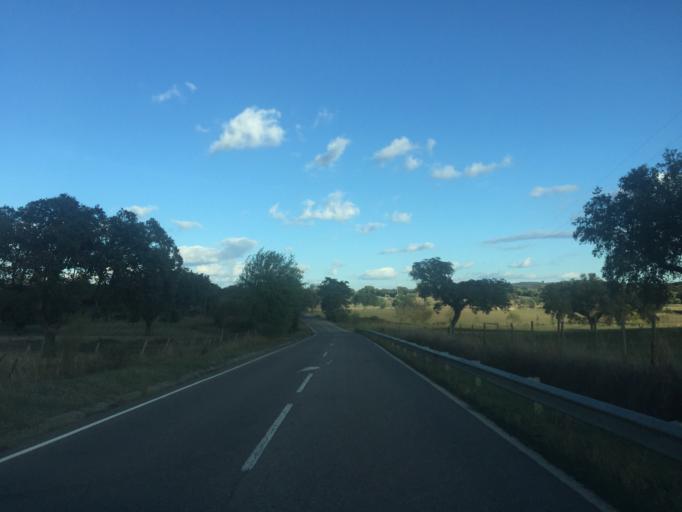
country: PT
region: Portalegre
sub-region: Alter do Chao
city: Alter do Chao
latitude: 39.1957
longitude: -7.6864
